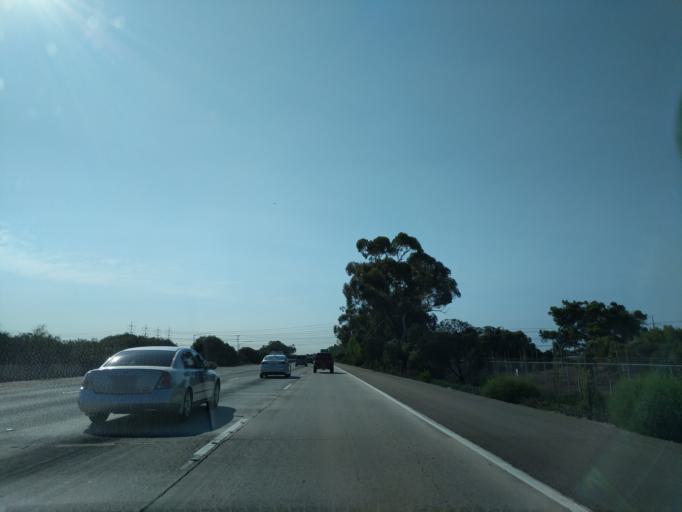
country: US
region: California
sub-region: San Diego County
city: Carlsbad
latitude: 33.1405
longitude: -117.3326
